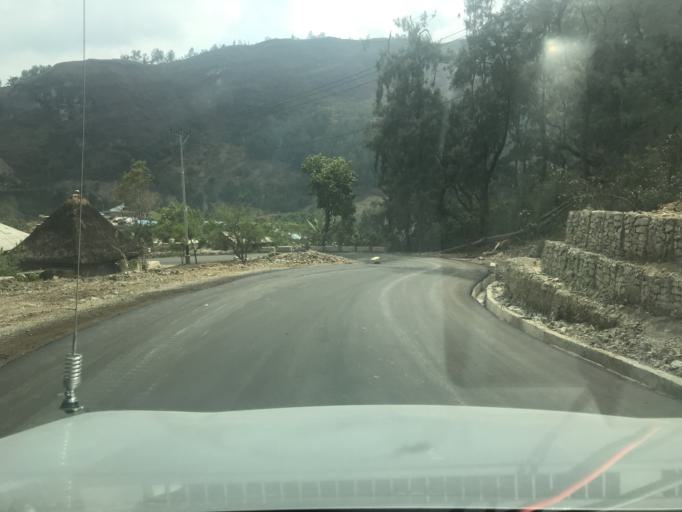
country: TL
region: Manufahi
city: Same
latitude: -8.8954
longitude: 125.5920
